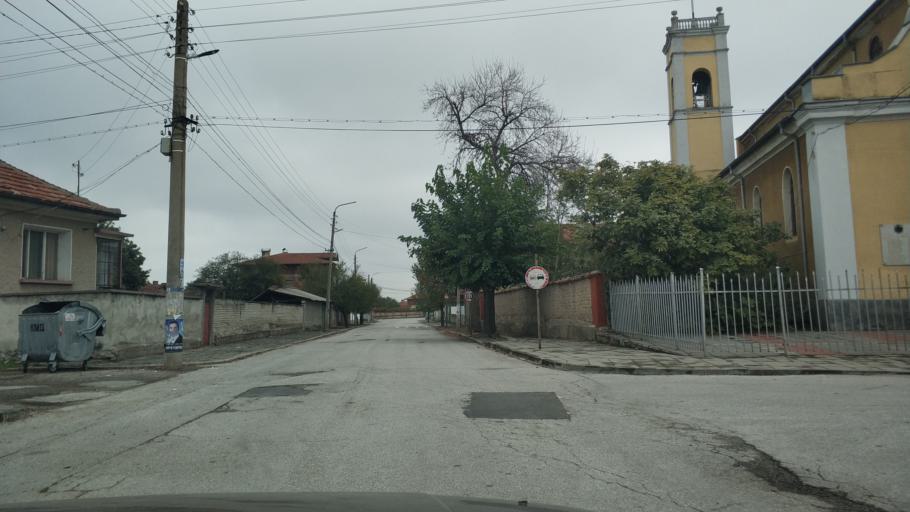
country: BG
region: Plovdiv
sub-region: Obshtina Kaloyanovo
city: Kaloyanovo
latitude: 42.3703
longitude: 24.7213
